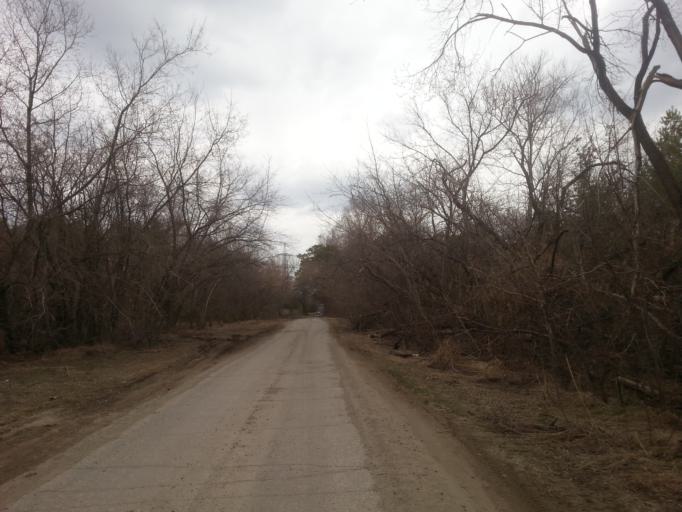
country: RU
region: Altai Krai
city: Yuzhnyy
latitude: 53.2865
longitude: 83.7303
